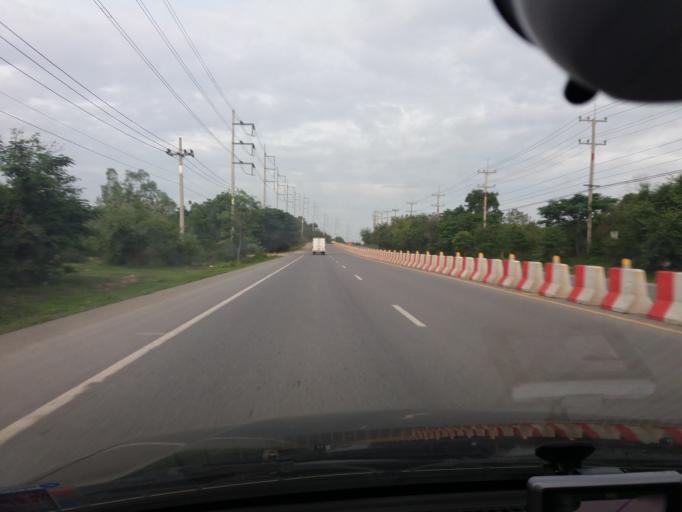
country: TH
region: Suphan Buri
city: U Thong
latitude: 14.3396
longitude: 99.8439
